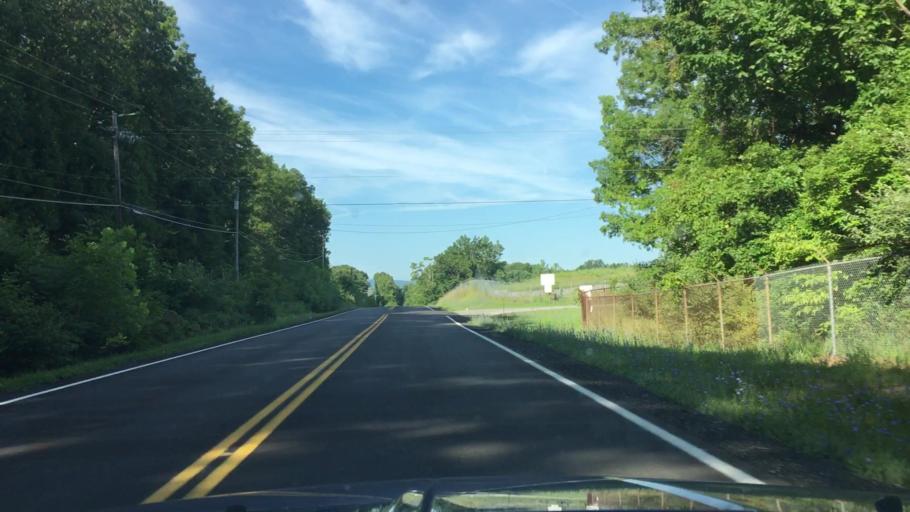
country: US
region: Virginia
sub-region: Augusta County
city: Lyndhurst
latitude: 38.0388
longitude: -78.9164
